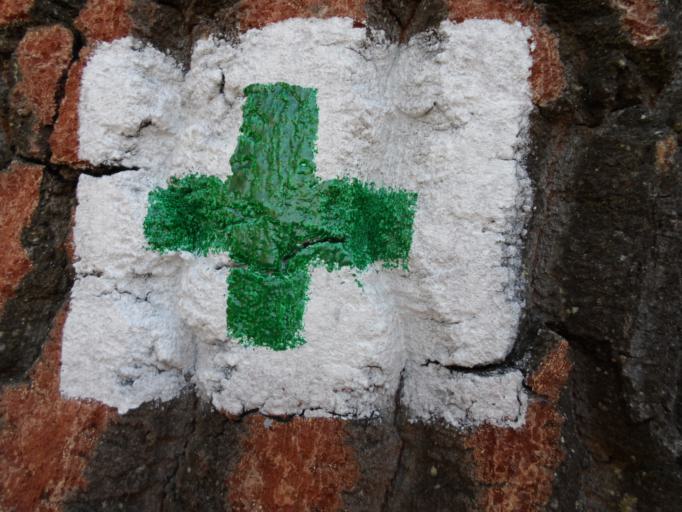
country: HU
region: Veszprem
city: Ajka
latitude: 47.2053
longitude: 17.5753
